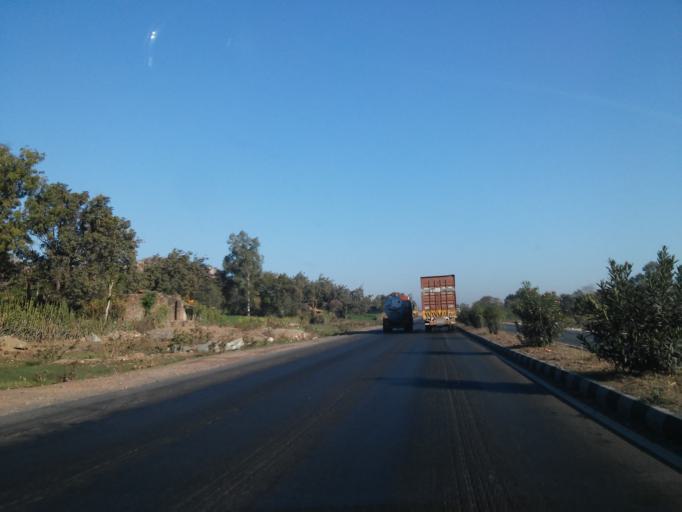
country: IN
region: Rajasthan
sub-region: Dungarpur
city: Dungarpur
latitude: 24.0221
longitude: 73.6588
